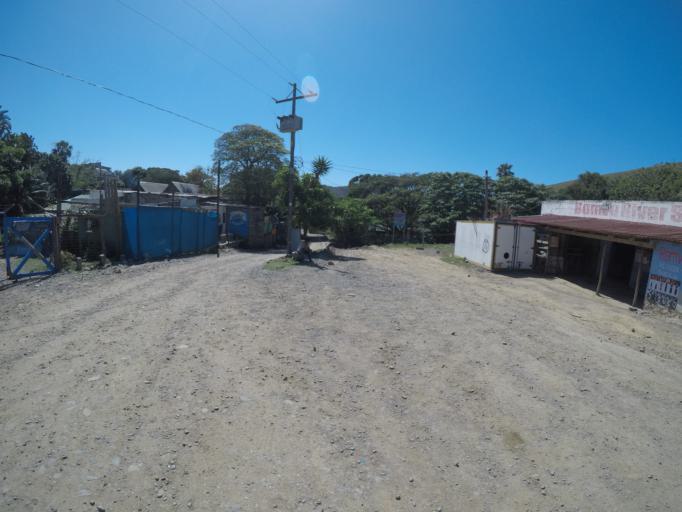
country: ZA
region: Eastern Cape
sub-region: OR Tambo District Municipality
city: Libode
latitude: -31.9888
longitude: 29.1460
